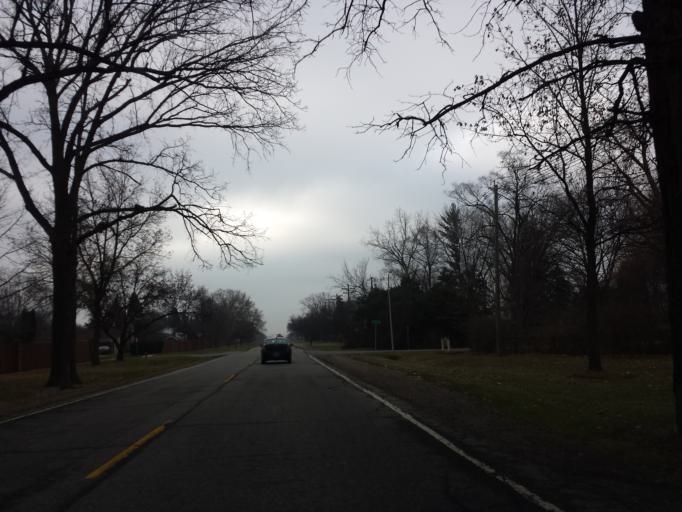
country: US
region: Michigan
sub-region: Oakland County
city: Lathrup Village
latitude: 42.5068
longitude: -83.2422
